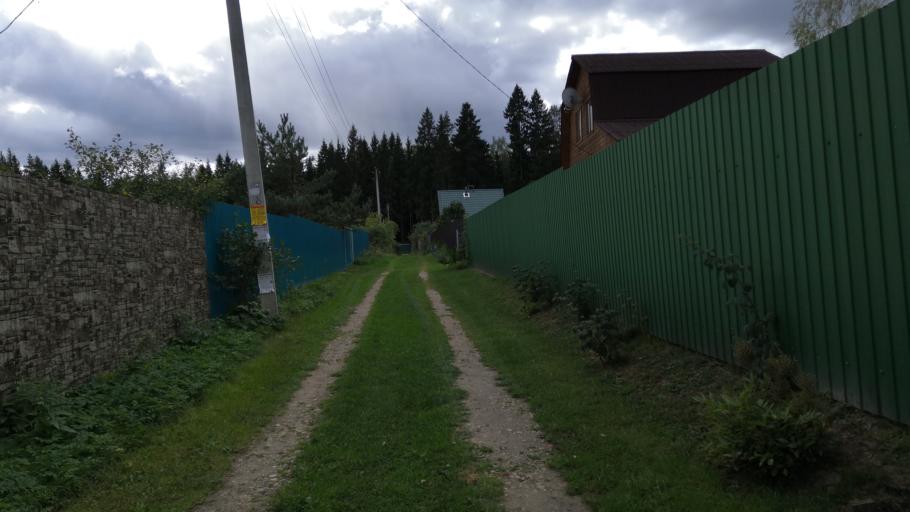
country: RU
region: Moskovskaya
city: Povarovo
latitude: 56.0543
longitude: 37.0223
